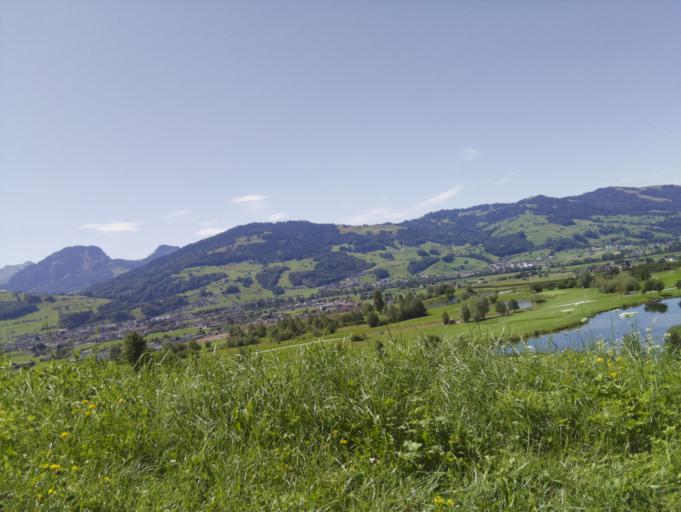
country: CH
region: Schwyz
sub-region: Bezirk March
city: Schubelbach
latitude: 47.1993
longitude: 8.9058
